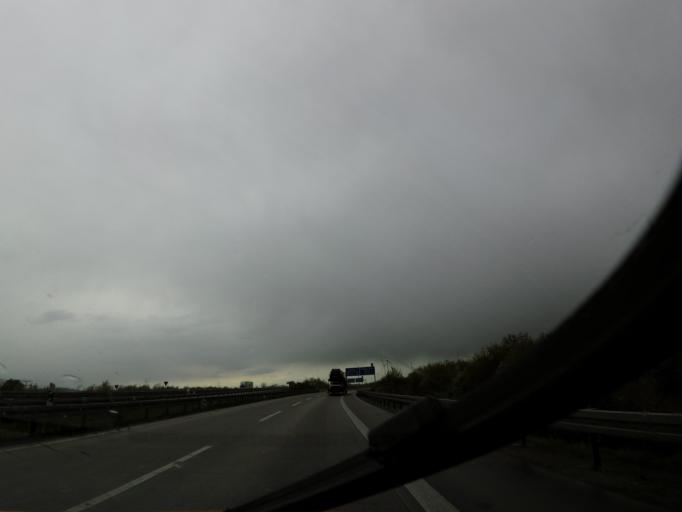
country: DE
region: Saxony-Anhalt
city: Dahlenwarsleben
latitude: 52.1614
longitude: 11.5450
